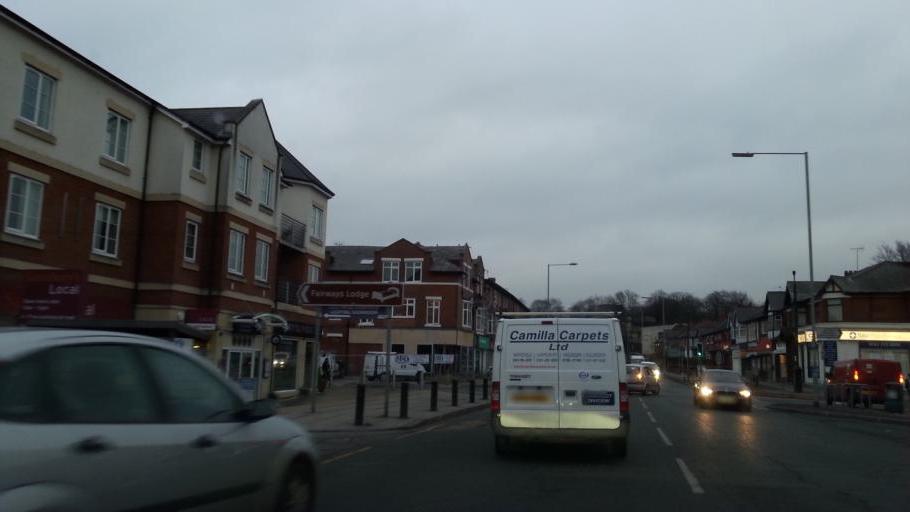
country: GB
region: England
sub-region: Borough of Bury
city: Prestwich
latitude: 53.5184
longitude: -2.2718
